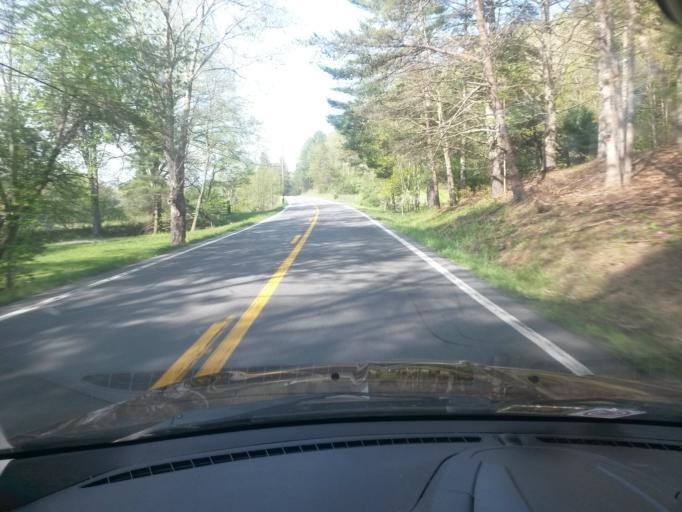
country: US
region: Virginia
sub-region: City of Covington
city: Covington
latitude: 37.9932
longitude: -80.0818
